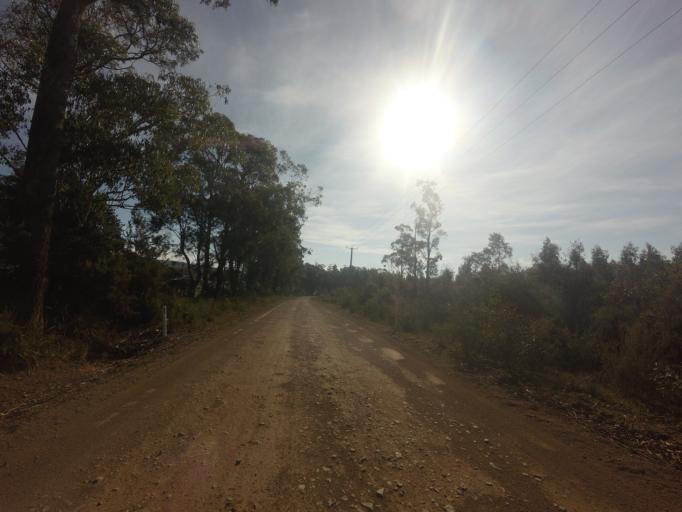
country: AU
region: Tasmania
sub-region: Sorell
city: Sorell
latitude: -42.4977
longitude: 147.5299
